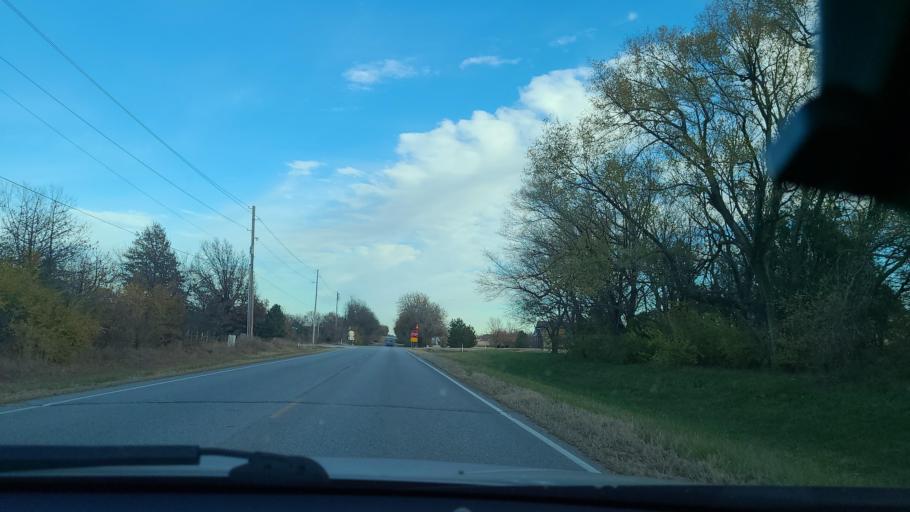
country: US
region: Kansas
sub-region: Sedgwick County
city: Goddard
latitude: 37.6497
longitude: -97.5545
